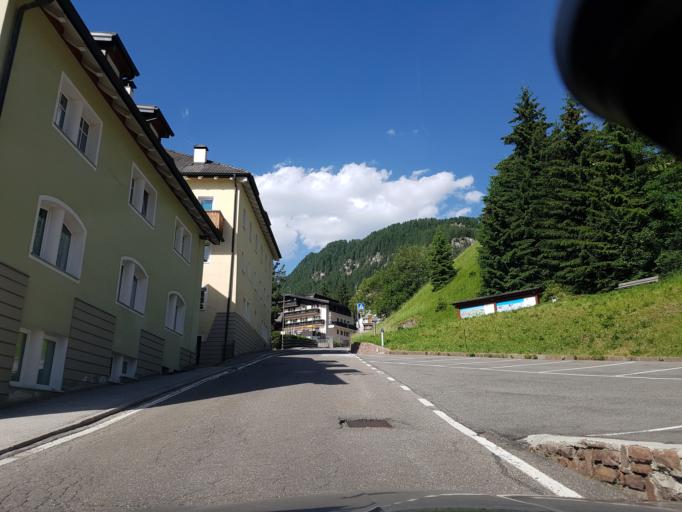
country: IT
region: Trentino-Alto Adige
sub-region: Bolzano
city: Santa Cristina Valgardena
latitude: 46.5597
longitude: 11.7295
